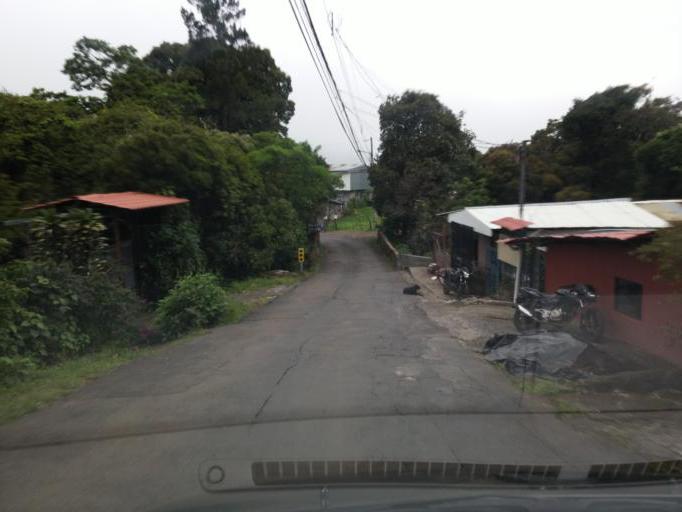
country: CR
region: Heredia
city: San Josecito
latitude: 10.0400
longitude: -84.1067
